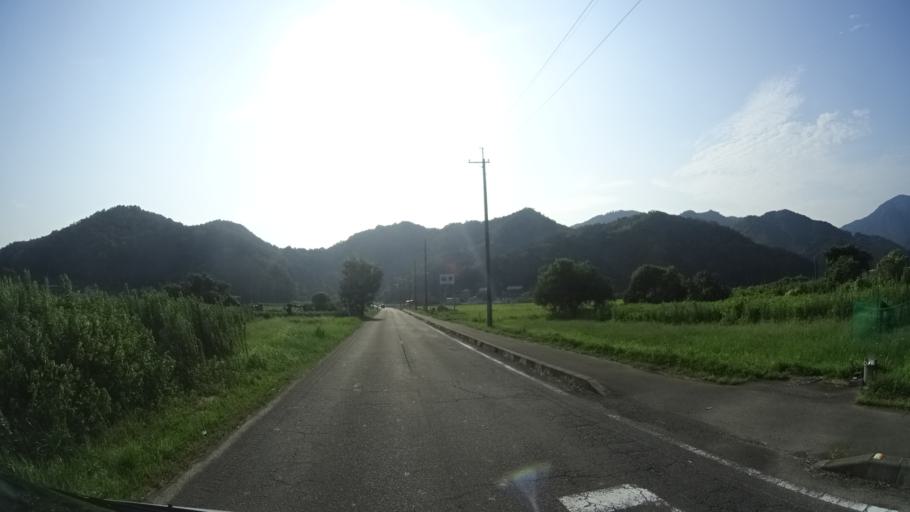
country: JP
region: Kyoto
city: Maizuru
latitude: 35.4659
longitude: 135.2814
